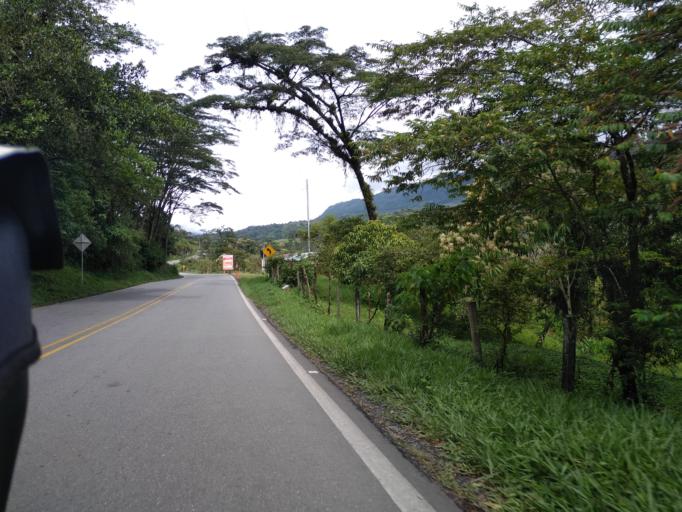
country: CO
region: Santander
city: Suaita
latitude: 6.0993
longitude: -73.3771
